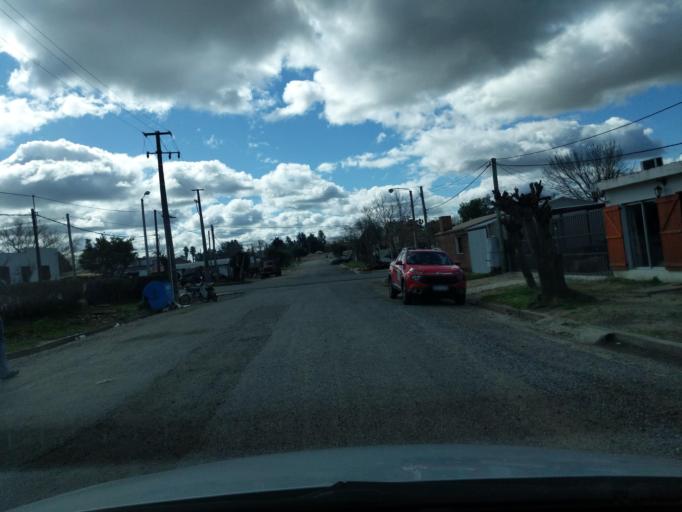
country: UY
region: Florida
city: Florida
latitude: -34.0853
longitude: -56.2186
